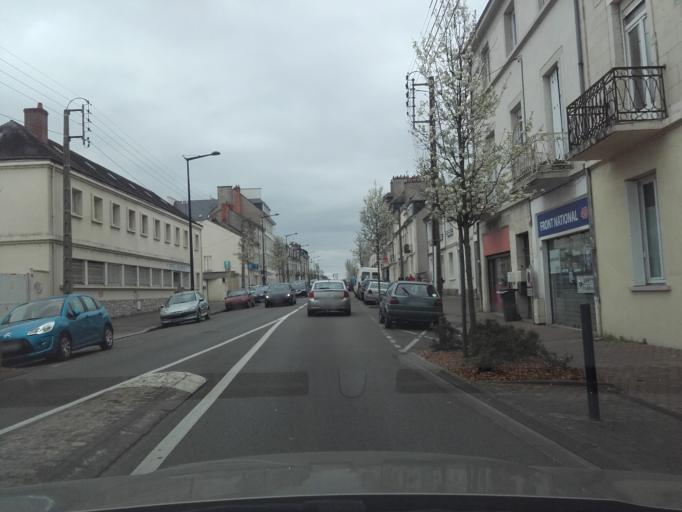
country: FR
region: Pays de la Loire
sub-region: Departement de Maine-et-Loire
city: Saumur
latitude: 47.2696
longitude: -0.0672
